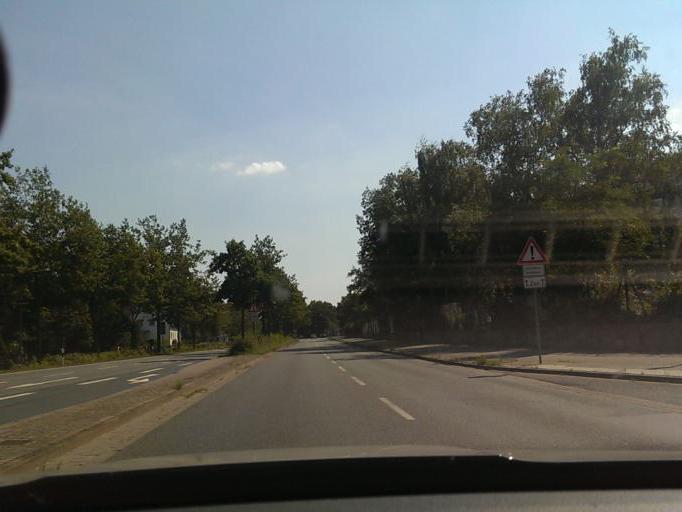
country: DE
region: Lower Saxony
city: Langenhagen
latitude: 52.4349
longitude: 9.7573
